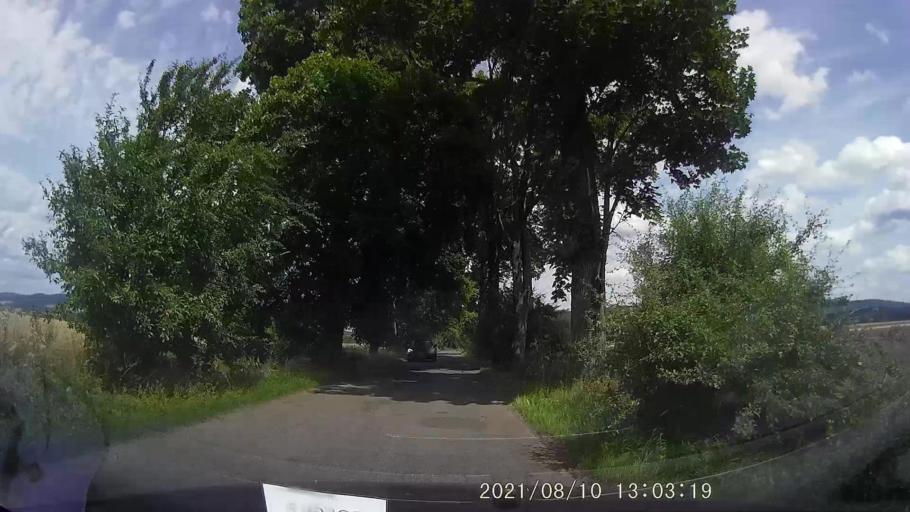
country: PL
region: Lower Silesian Voivodeship
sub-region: Powiat klodzki
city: Bozkow
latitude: 50.4701
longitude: 16.5612
